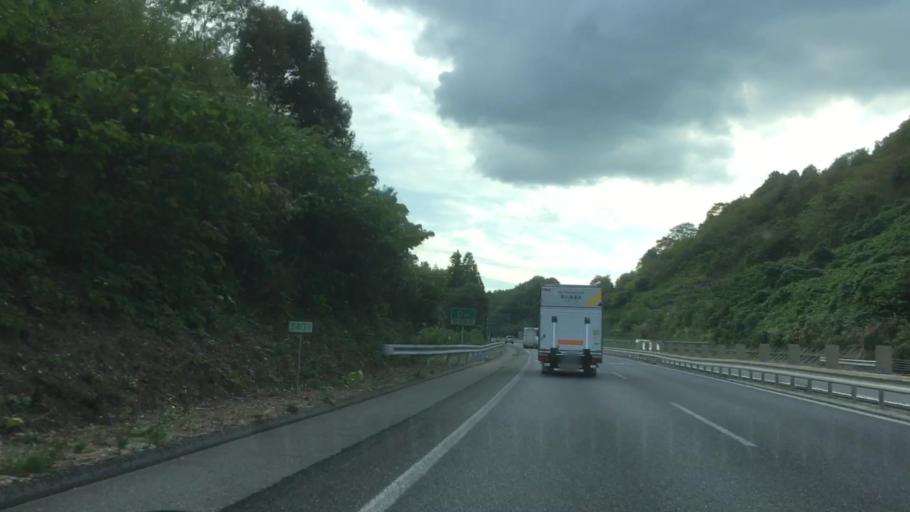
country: JP
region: Yamaguchi
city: Iwakuni
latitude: 34.1308
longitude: 132.1125
